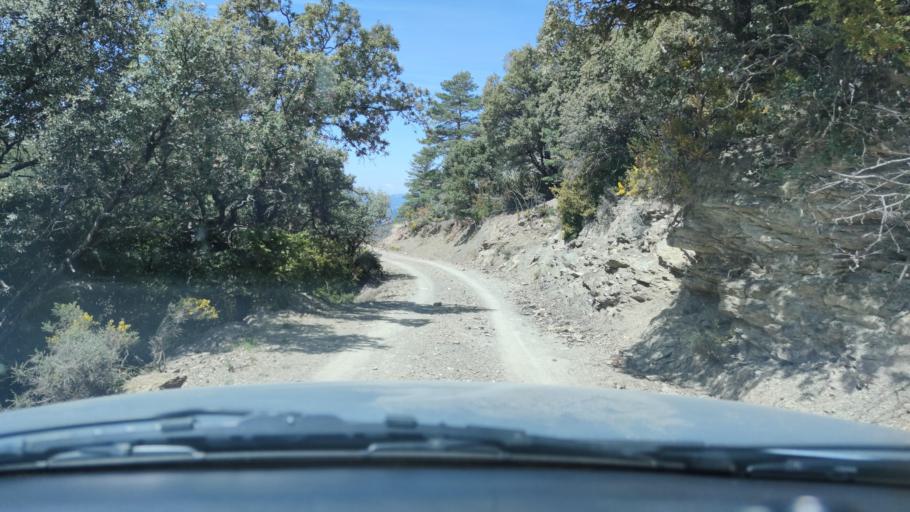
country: ES
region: Catalonia
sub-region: Provincia de Lleida
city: Sort
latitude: 42.3096
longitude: 1.1513
